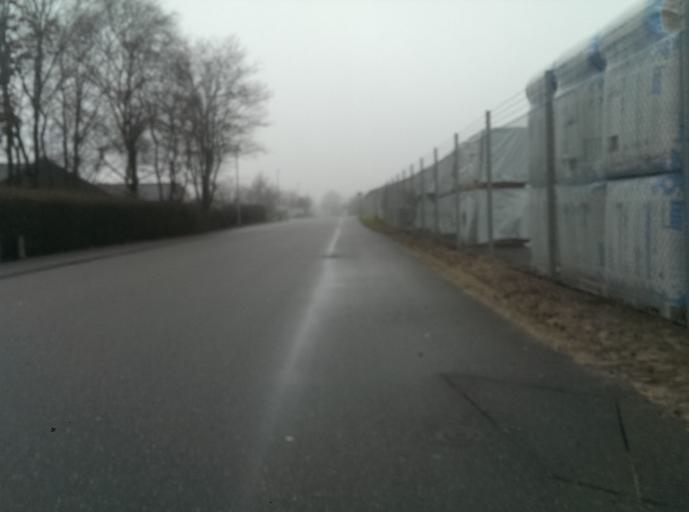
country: DK
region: South Denmark
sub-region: Esbjerg Kommune
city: Bramming
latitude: 55.4660
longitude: 8.6817
